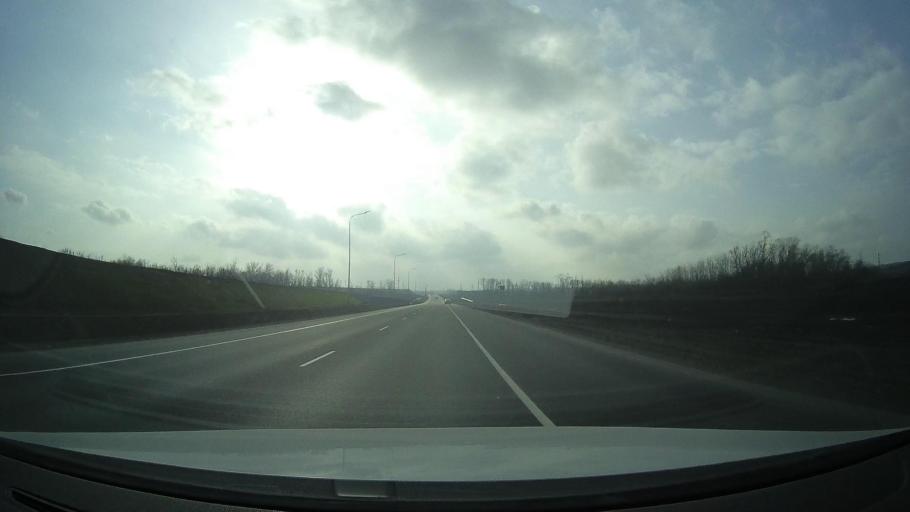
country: RU
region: Rostov
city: Grushevskaya
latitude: 47.4217
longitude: 39.8632
